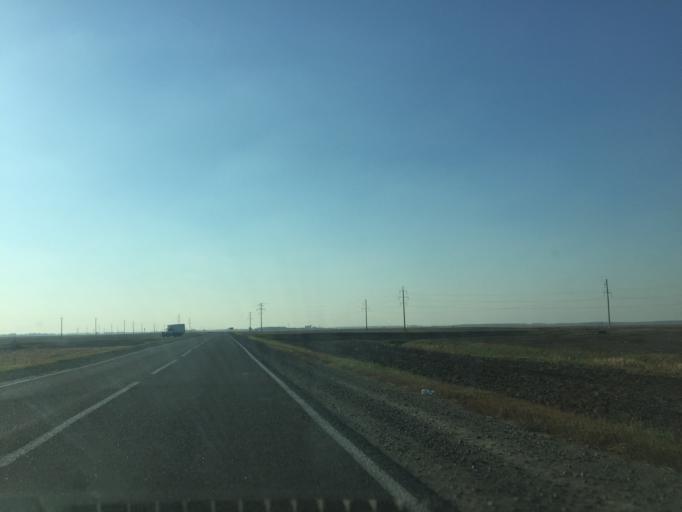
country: BY
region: Gomel
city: Dobrush
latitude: 52.3866
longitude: 31.4312
